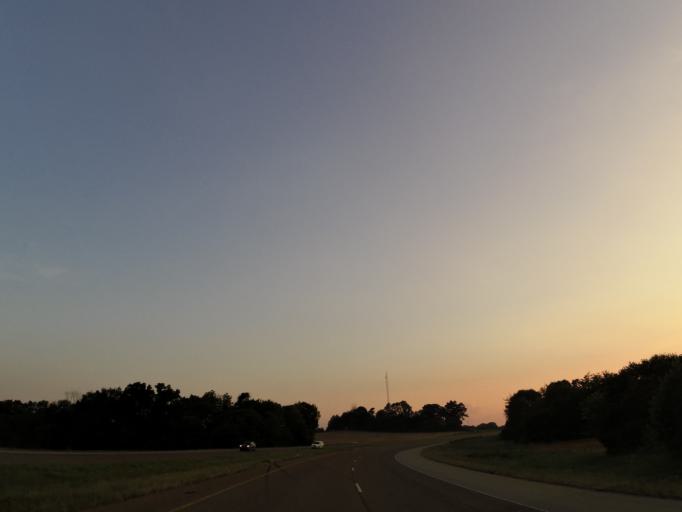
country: US
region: Tennessee
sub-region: Henry County
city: Paris
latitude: 36.2278
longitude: -88.3709
